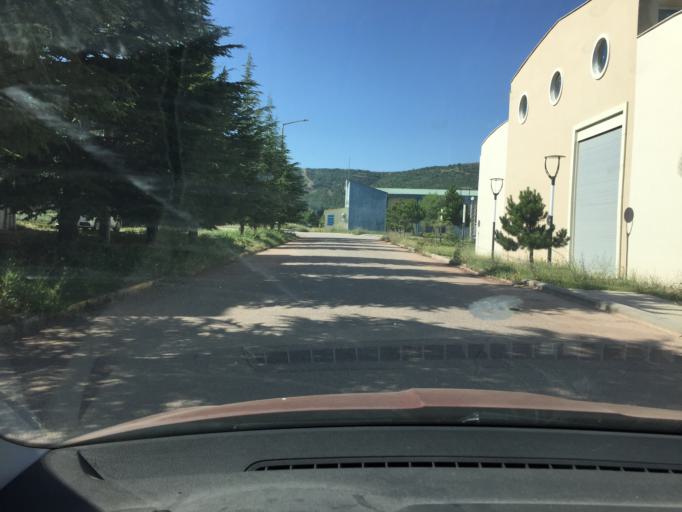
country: TR
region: Eskisehir
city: Eskisehir
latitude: 39.7477
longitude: 30.4749
